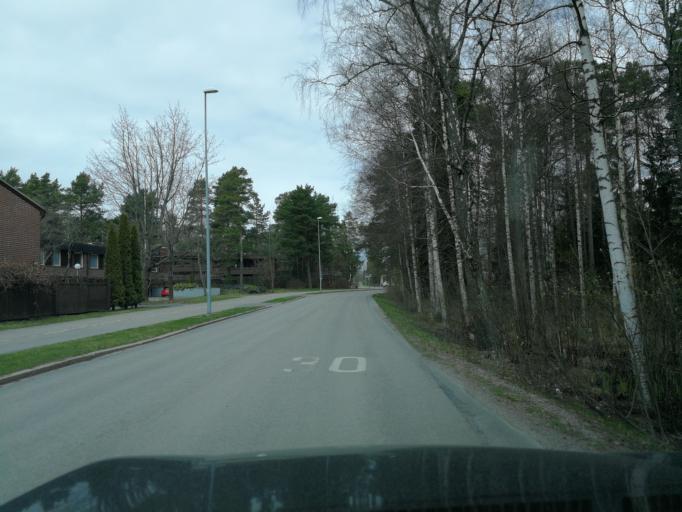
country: FI
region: Uusimaa
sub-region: Helsinki
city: Koukkuniemi
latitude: 60.1572
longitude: 24.7812
